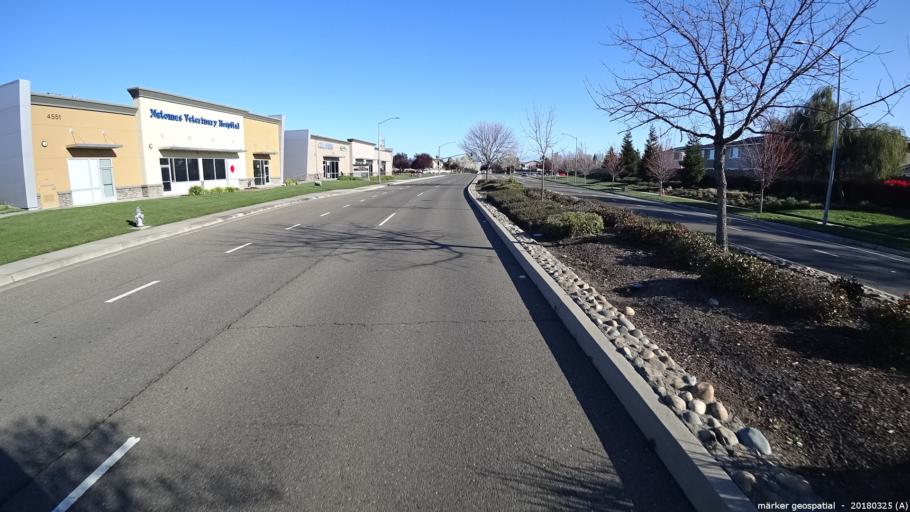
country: US
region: California
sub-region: Sacramento County
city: Rio Linda
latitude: 38.6553
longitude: -121.5030
